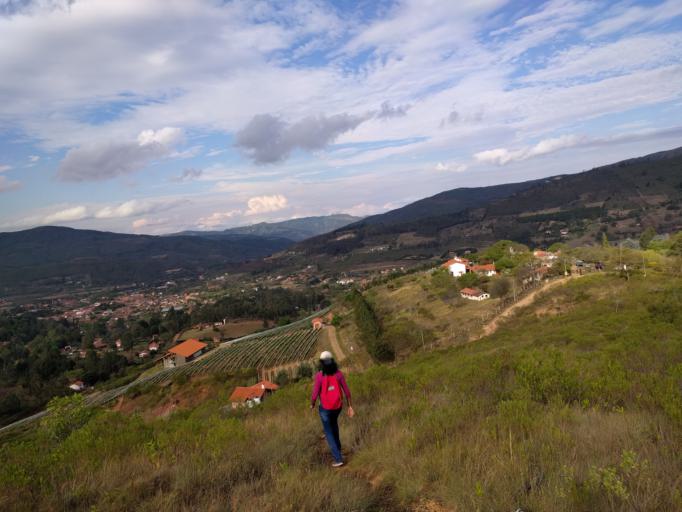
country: BO
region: Santa Cruz
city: Samaipata
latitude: -18.1888
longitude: -63.8860
